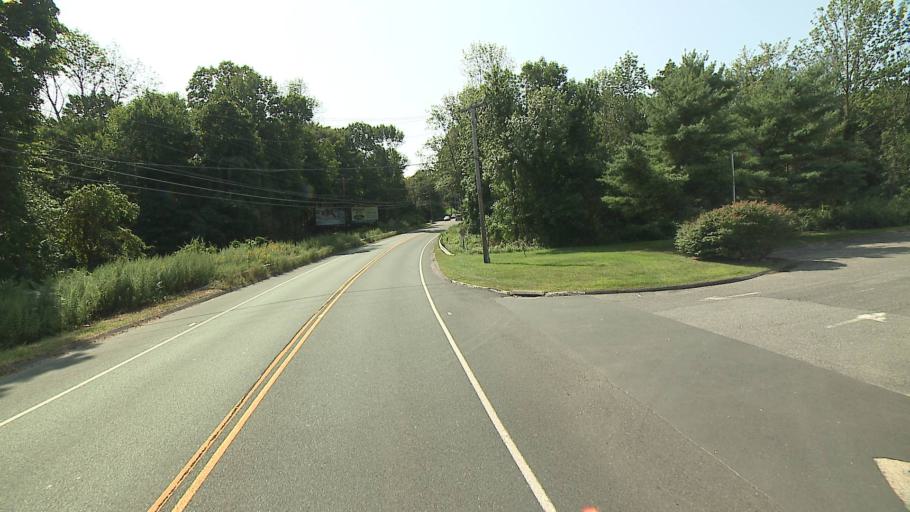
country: US
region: Connecticut
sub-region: Fairfield County
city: Newtown
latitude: 41.3542
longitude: -73.2608
